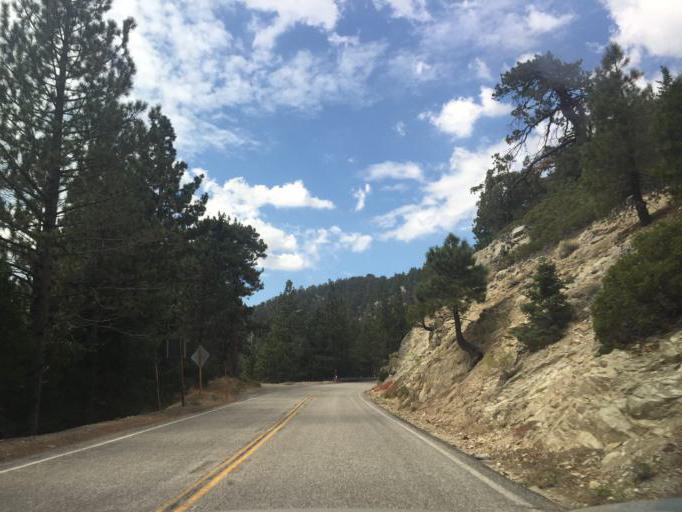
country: US
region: California
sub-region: Los Angeles County
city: Littlerock
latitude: 34.3446
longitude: -117.9095
